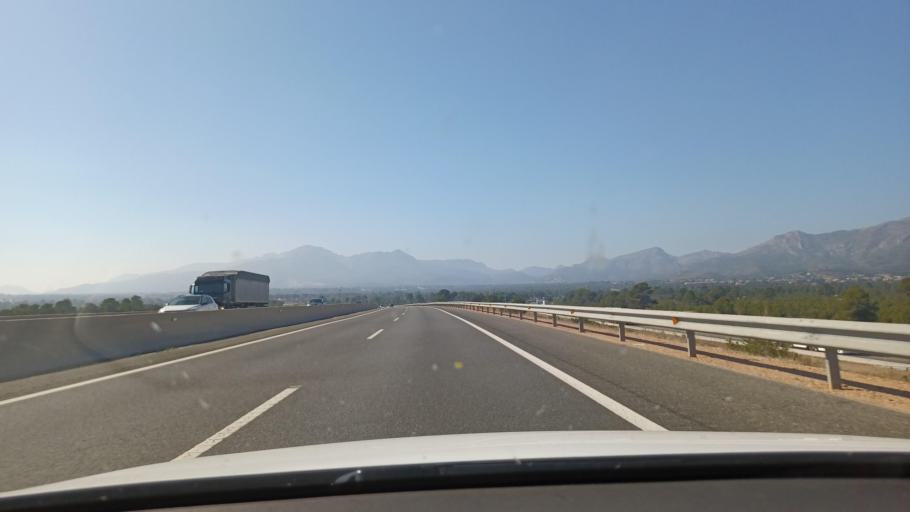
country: ES
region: Catalonia
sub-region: Provincia de Tarragona
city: Vilanova d'Escornalbou
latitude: 41.0389
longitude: 0.9522
